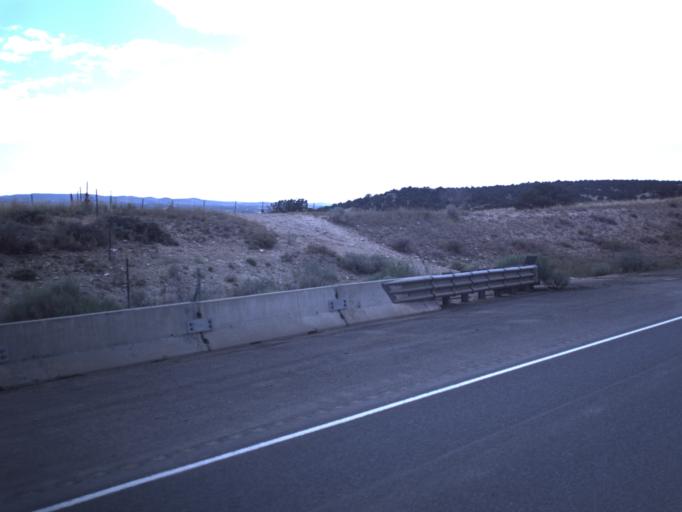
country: US
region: Utah
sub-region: Duchesne County
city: Duchesne
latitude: 40.1740
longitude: -110.4999
